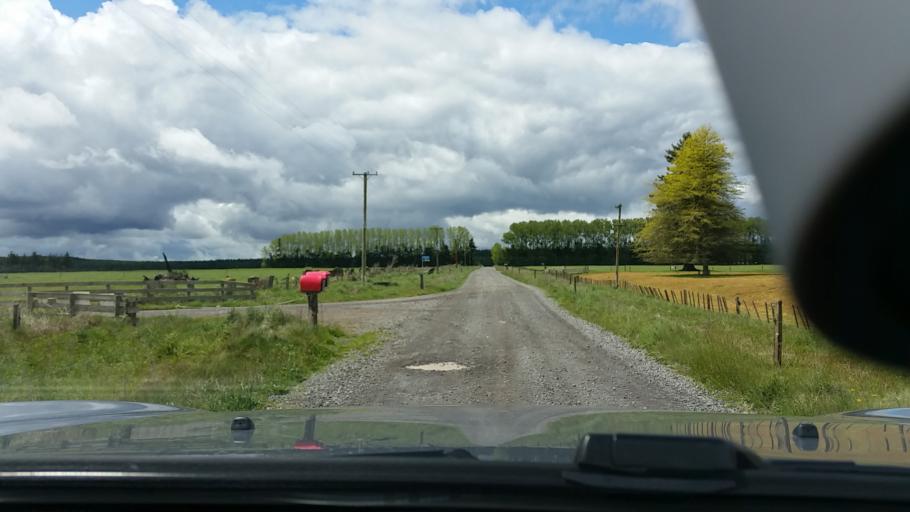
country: NZ
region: Bay of Plenty
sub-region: Whakatane District
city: Murupara
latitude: -38.4894
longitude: 176.4694
